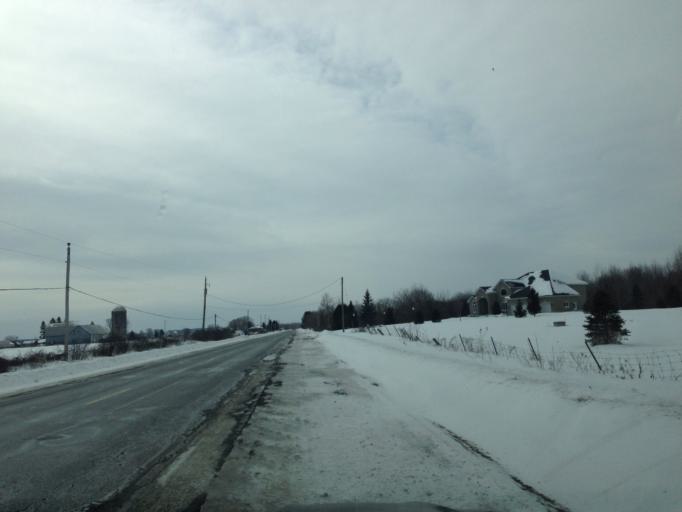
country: CA
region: Ontario
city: Ottawa
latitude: 45.3246
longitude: -75.5174
